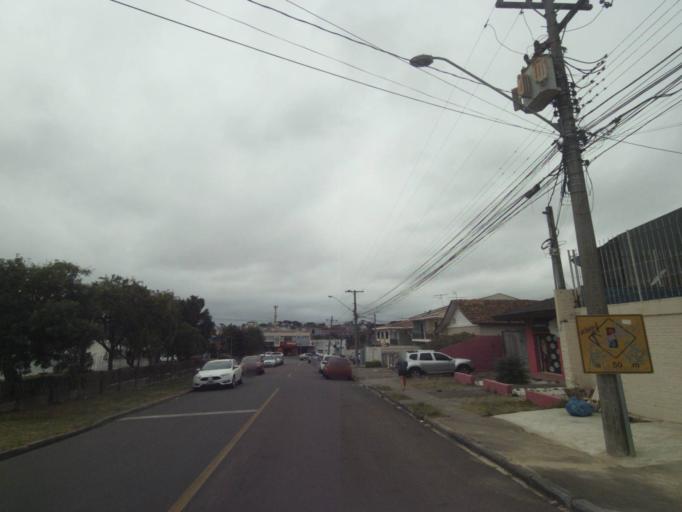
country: BR
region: Parana
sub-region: Pinhais
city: Pinhais
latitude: -25.4757
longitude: -49.2297
